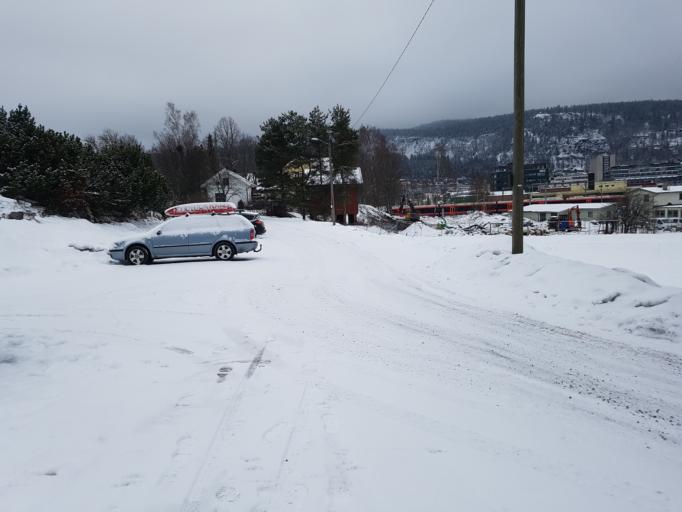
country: NO
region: Buskerud
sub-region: Drammen
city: Drammen
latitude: 59.7406
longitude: 10.1868
